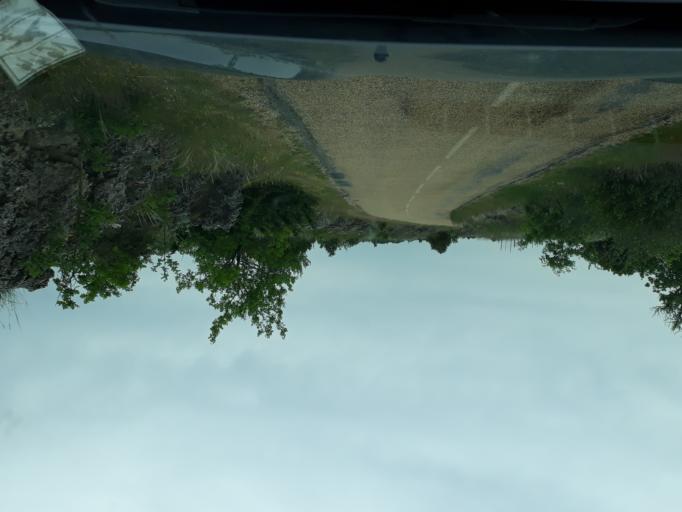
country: FR
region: Languedoc-Roussillon
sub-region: Departement de l'Herault
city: Lodeve
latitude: 43.8577
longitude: 3.2669
